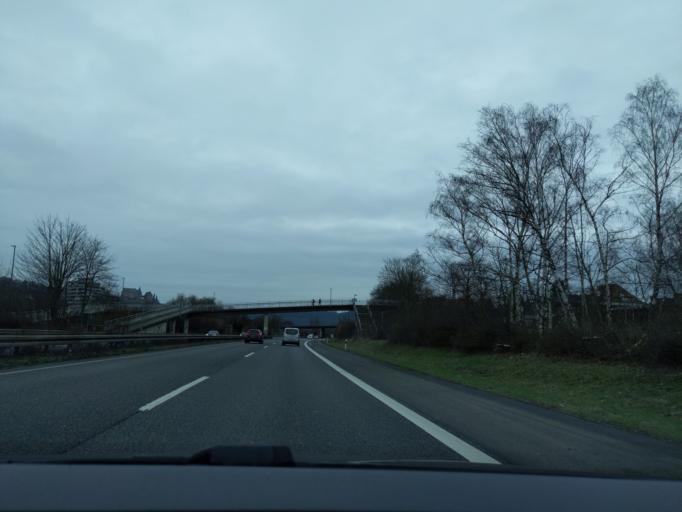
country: DE
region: Hesse
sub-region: Regierungsbezirk Giessen
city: Marburg an der Lahn
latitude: 50.7942
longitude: 8.7617
